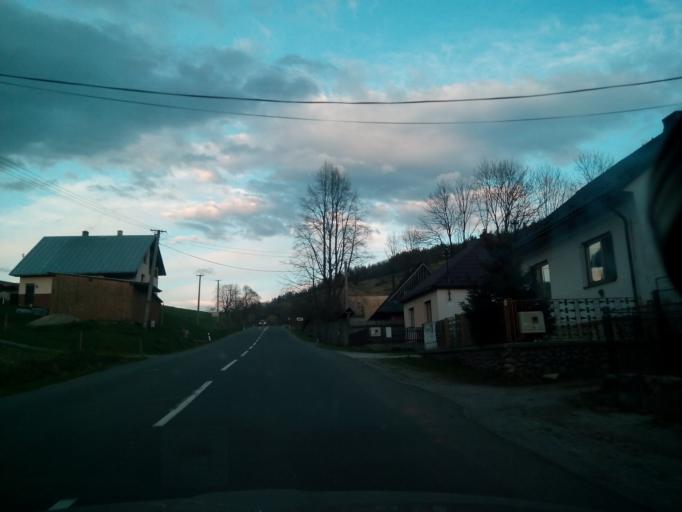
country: SK
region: Presovsky
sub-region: Okres Poprad
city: Zdiar
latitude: 49.2967
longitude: 20.3854
